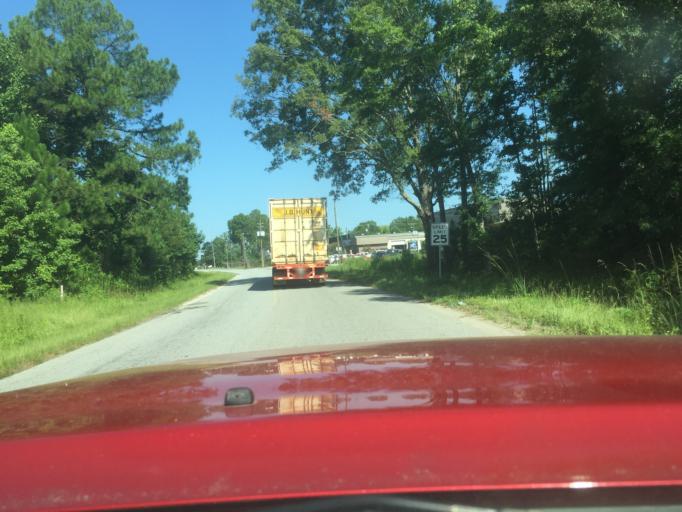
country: US
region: Georgia
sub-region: Chatham County
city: Garden City
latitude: 32.0776
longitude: -81.1505
